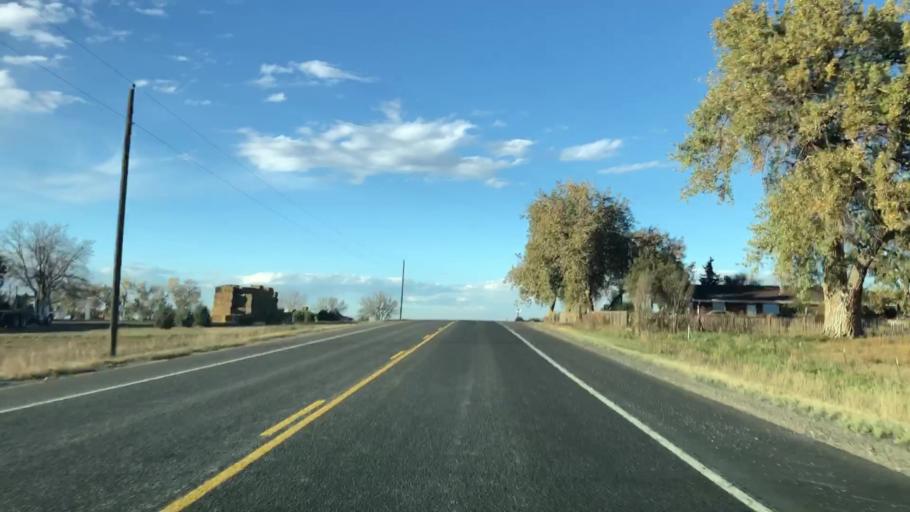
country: US
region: Colorado
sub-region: Larimer County
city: Loveland
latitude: 40.4715
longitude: -105.0203
